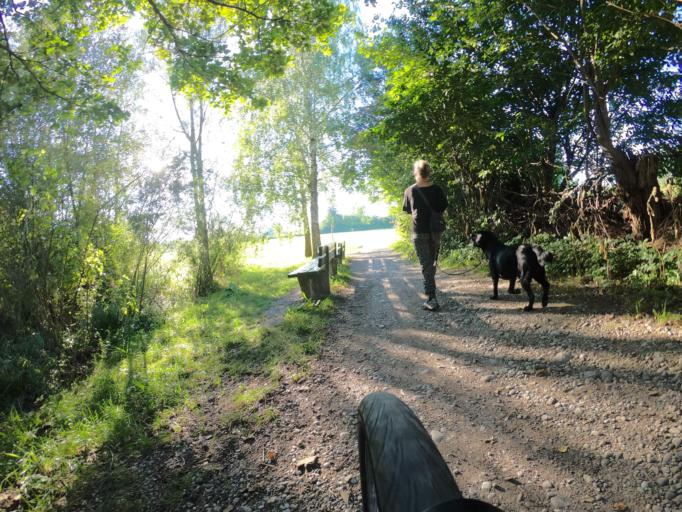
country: DE
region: Bavaria
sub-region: Upper Bavaria
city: Grobenzell
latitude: 48.1776
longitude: 11.3852
